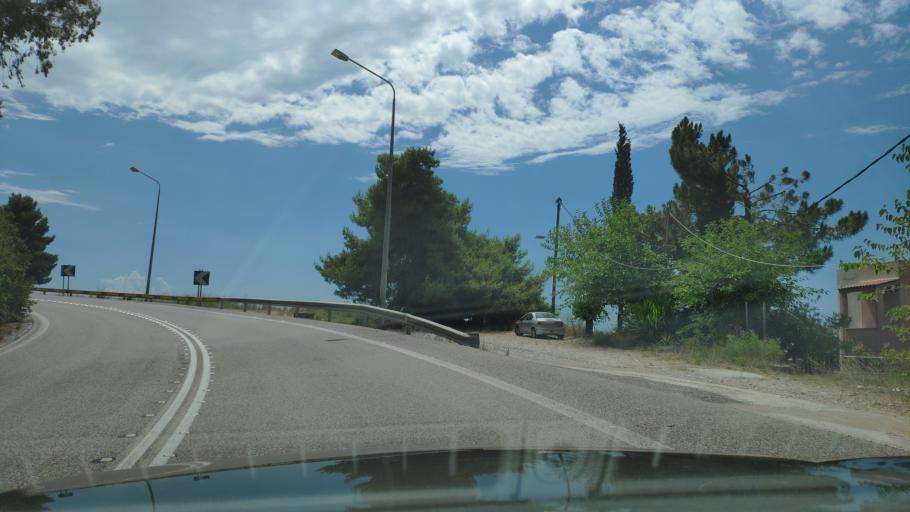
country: GR
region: West Greece
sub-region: Nomos Aitolias kai Akarnanias
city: Menidi
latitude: 39.0395
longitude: 21.1193
